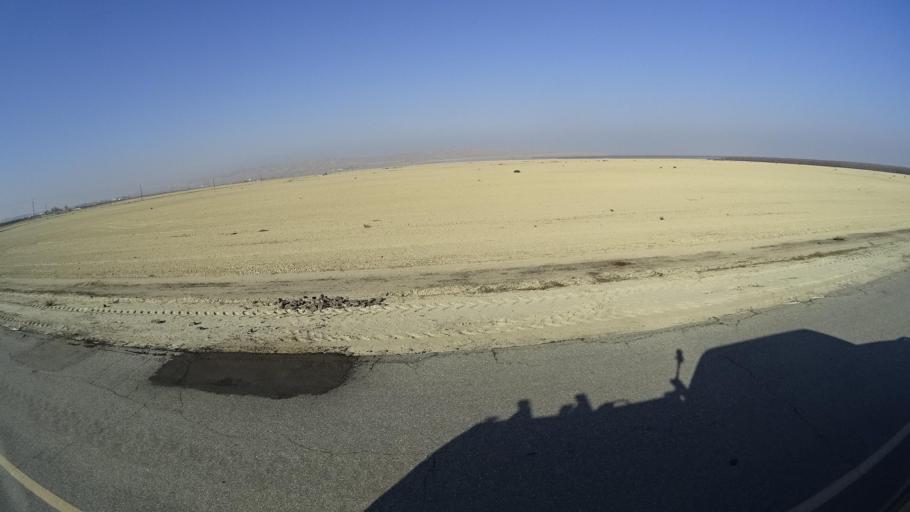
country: US
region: California
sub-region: Kern County
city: Maricopa
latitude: 35.1016
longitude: -119.3652
